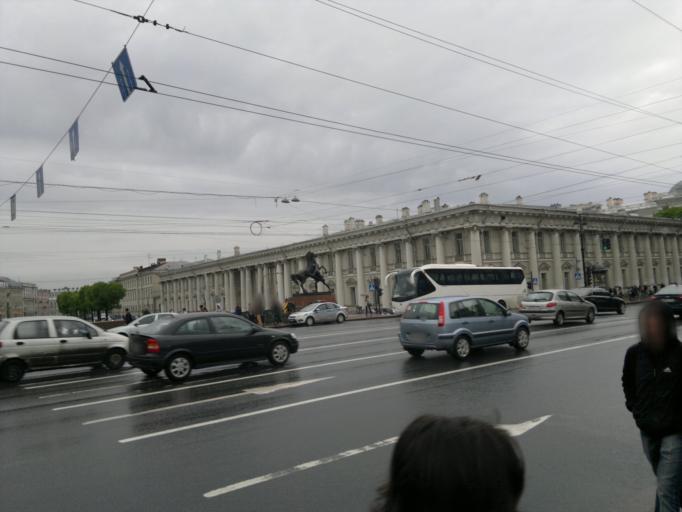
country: RU
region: St.-Petersburg
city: Centralniy
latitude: 59.9334
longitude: 30.3435
